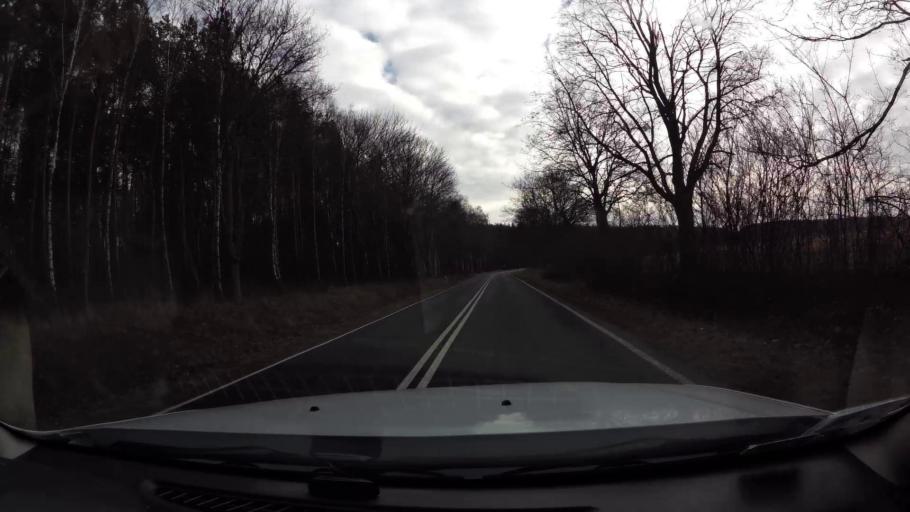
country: PL
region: West Pomeranian Voivodeship
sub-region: Powiat mysliborski
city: Debno
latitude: 52.7758
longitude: 14.6610
